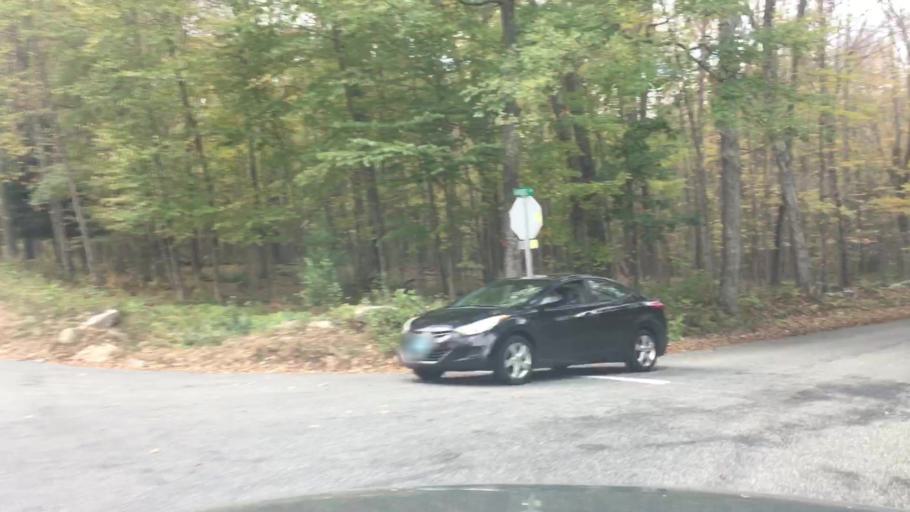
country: US
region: Connecticut
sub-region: Tolland County
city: Storrs
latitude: 41.8769
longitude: -72.1688
